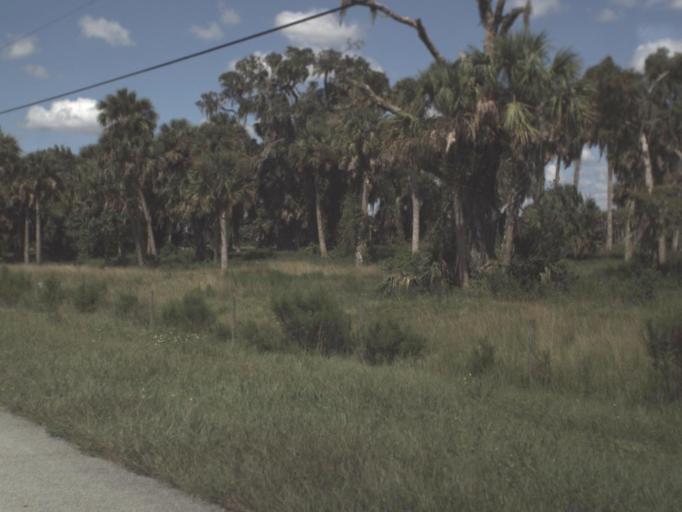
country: US
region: Florida
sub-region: Okeechobee County
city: Taylor Creek
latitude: 27.1754
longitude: -80.7283
